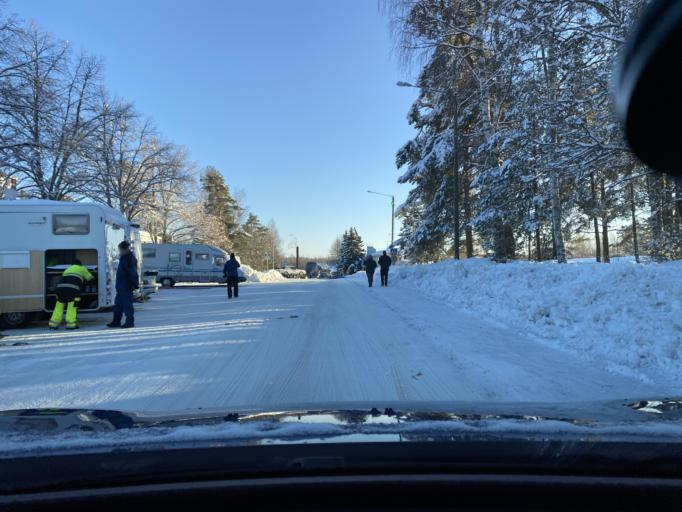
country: FI
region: Southern Savonia
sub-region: Mikkeli
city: Kangasniemi
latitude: 61.9897
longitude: 26.6350
